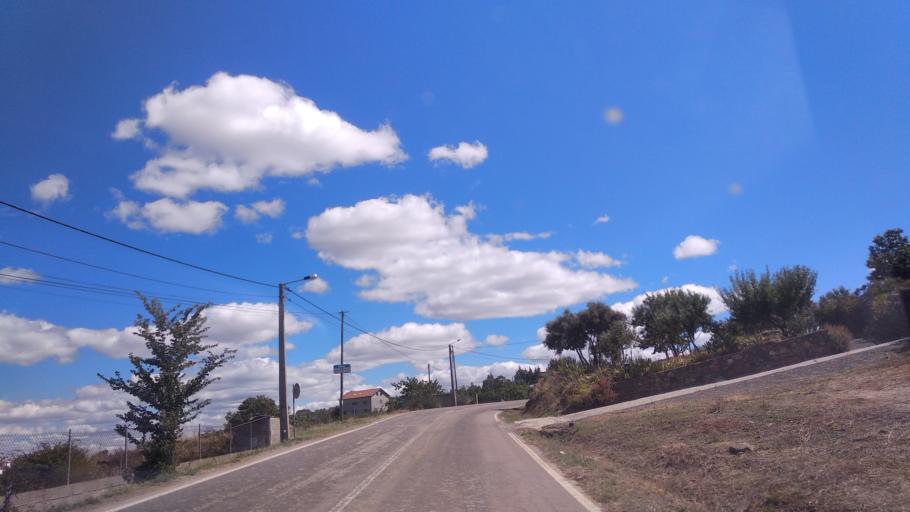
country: PT
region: Braganca
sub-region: Braganca Municipality
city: Braganca
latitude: 41.7821
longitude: -6.7649
